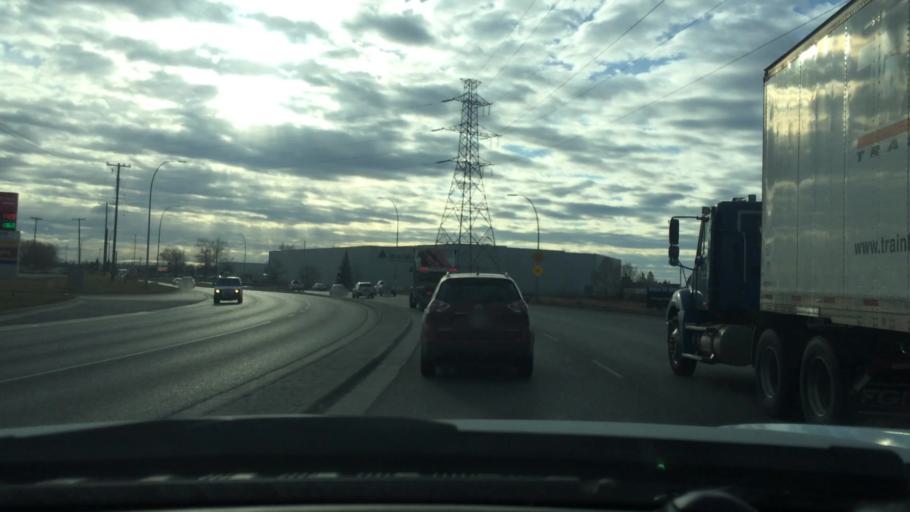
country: CA
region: Alberta
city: Calgary
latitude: 51.0082
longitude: -114.0014
